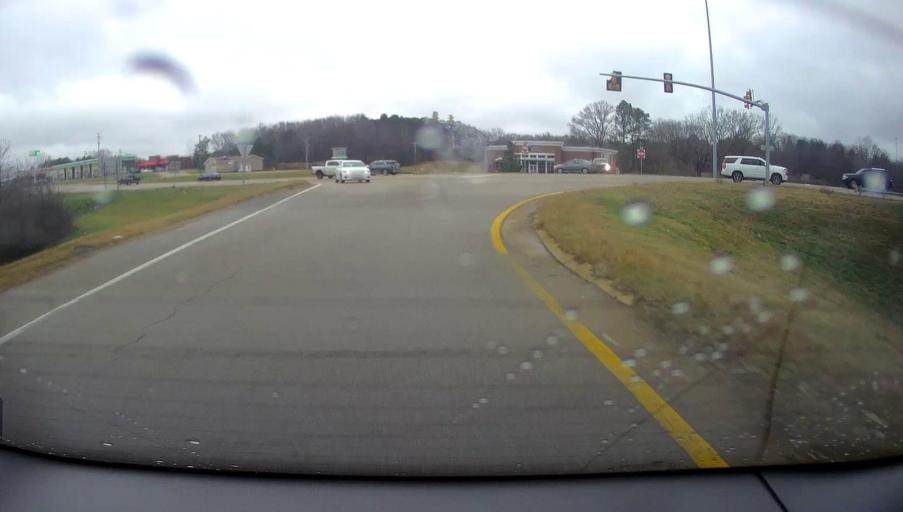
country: US
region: Mississippi
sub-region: Alcorn County
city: Corinth
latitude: 34.9307
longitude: -88.5482
